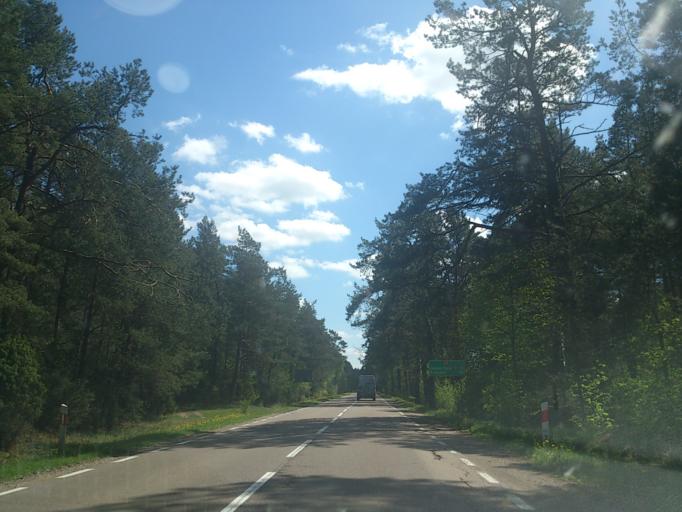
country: PL
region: Podlasie
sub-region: Powiat zambrowski
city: Rutki
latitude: 53.2040
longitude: 22.5512
